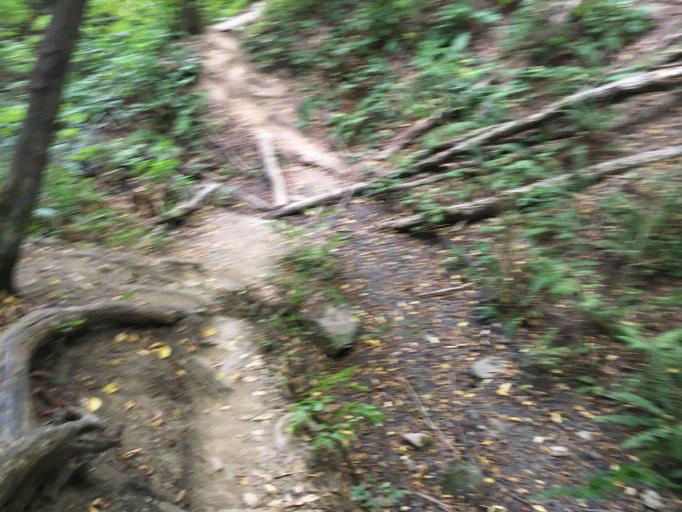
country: RU
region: Krasnodarskiy
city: Tuapse
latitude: 44.2513
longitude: 39.2301
